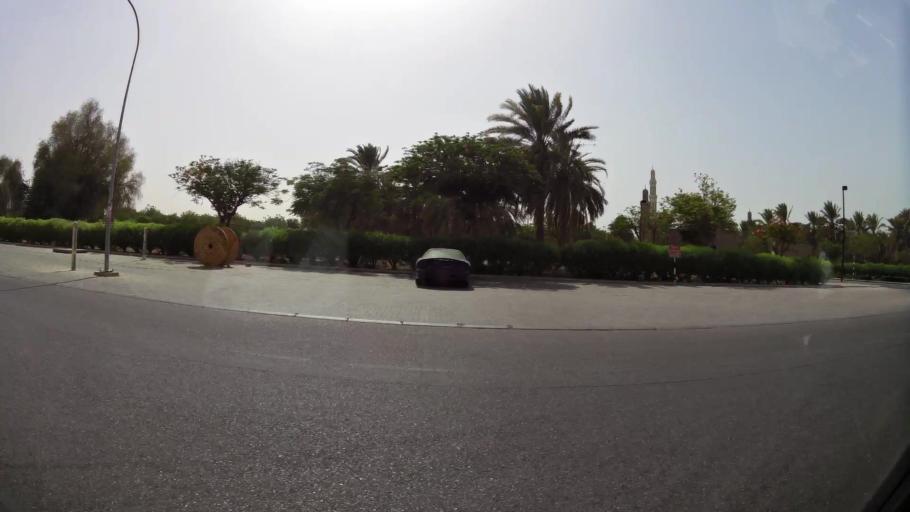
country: OM
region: Muhafazat Masqat
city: Bawshar
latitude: 23.5815
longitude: 58.3920
